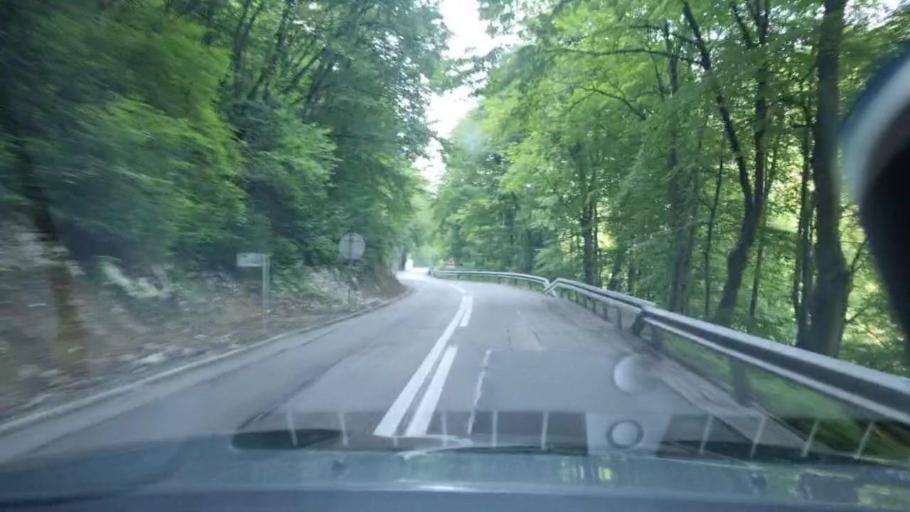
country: BA
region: Federation of Bosnia and Herzegovina
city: Stijena
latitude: 44.8871
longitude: 16.0572
